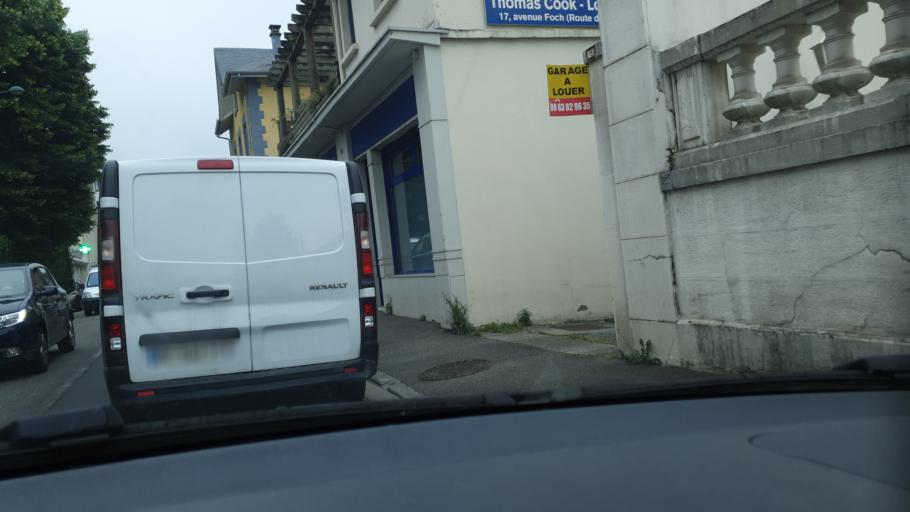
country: FR
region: Midi-Pyrenees
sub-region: Departement des Hautes-Pyrenees
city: Lourdes
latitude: 43.0900
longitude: -0.0461
